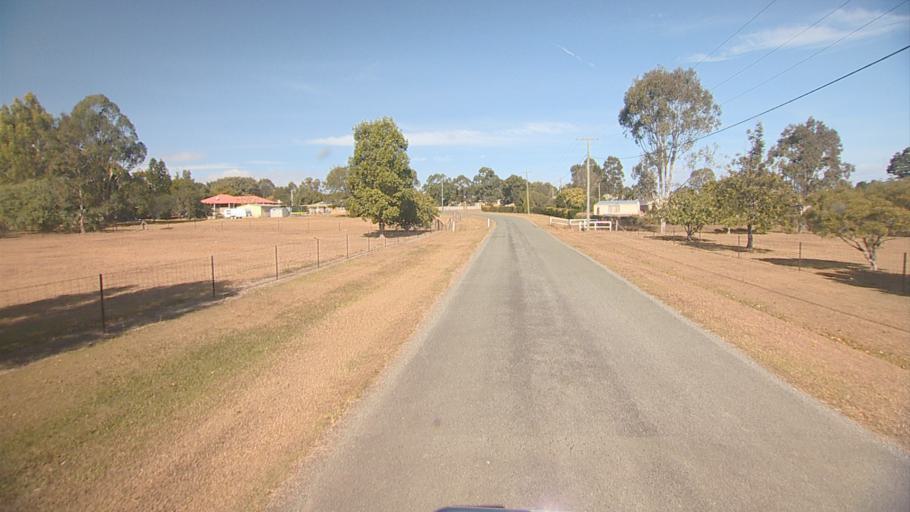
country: AU
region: Queensland
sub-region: Logan
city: Cedar Vale
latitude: -27.8687
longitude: 152.9687
